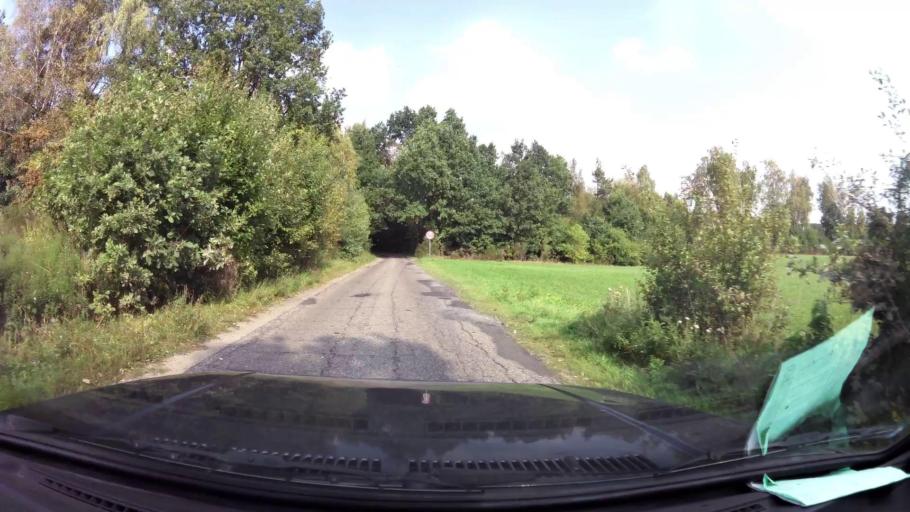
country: PL
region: West Pomeranian Voivodeship
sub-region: Powiat koszalinski
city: Polanow
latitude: 54.1269
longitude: 16.5187
